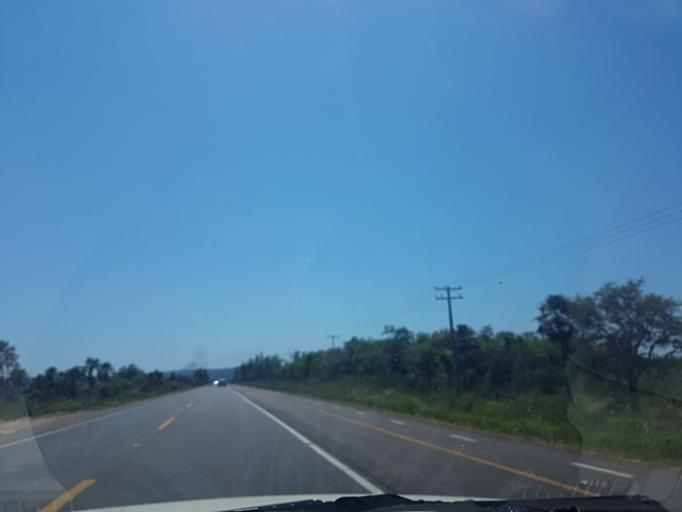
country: PY
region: Cordillera
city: Emboscada
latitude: -25.2087
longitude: -57.3927
